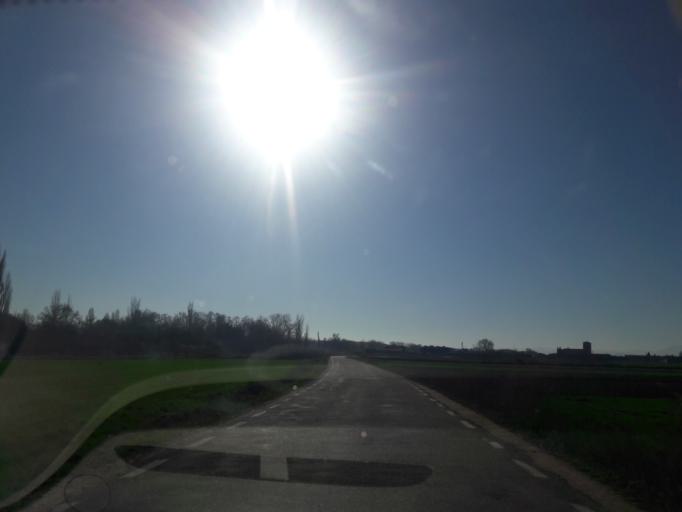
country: ES
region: Castille and Leon
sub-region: Provincia de Salamanca
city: Tordillos
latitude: 40.8592
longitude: -5.3593
